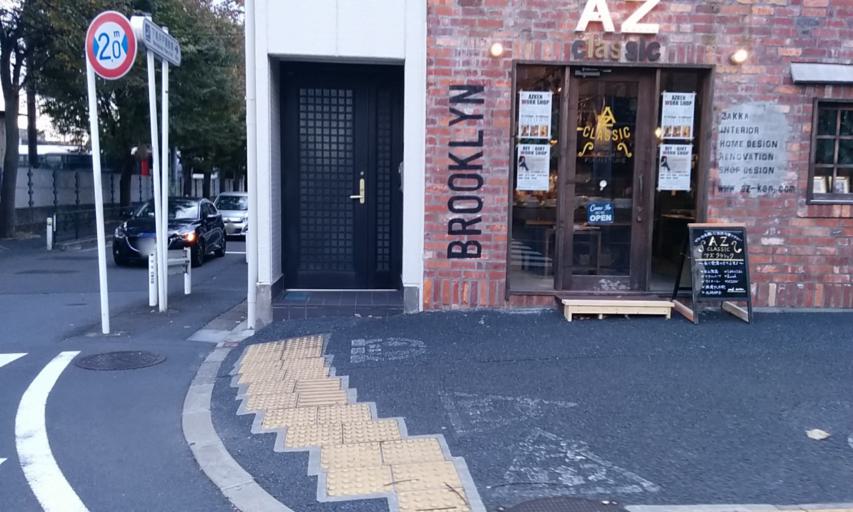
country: JP
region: Tokyo
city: Tokyo
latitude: 35.6779
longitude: 139.6405
